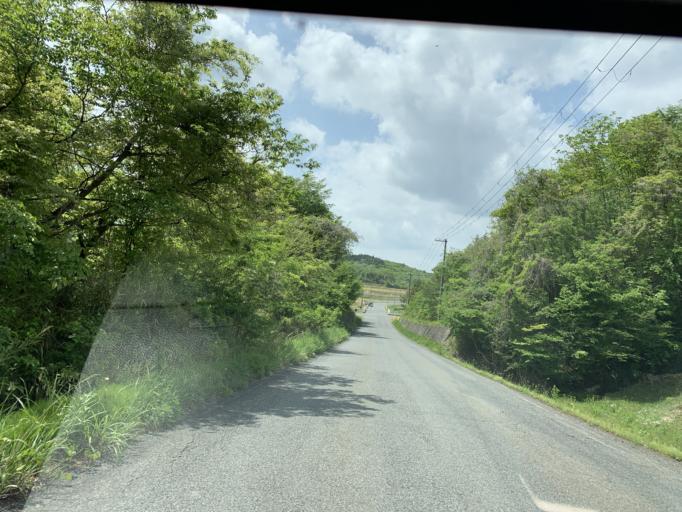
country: JP
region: Miyagi
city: Furukawa
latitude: 38.7699
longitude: 140.9538
